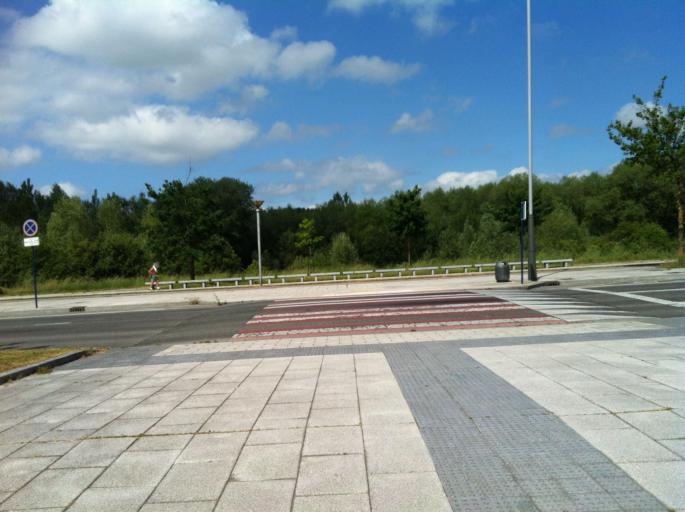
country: ES
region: Basque Country
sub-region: Provincia de Alava
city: Gasteiz / Vitoria
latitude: 42.8570
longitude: -2.6514
